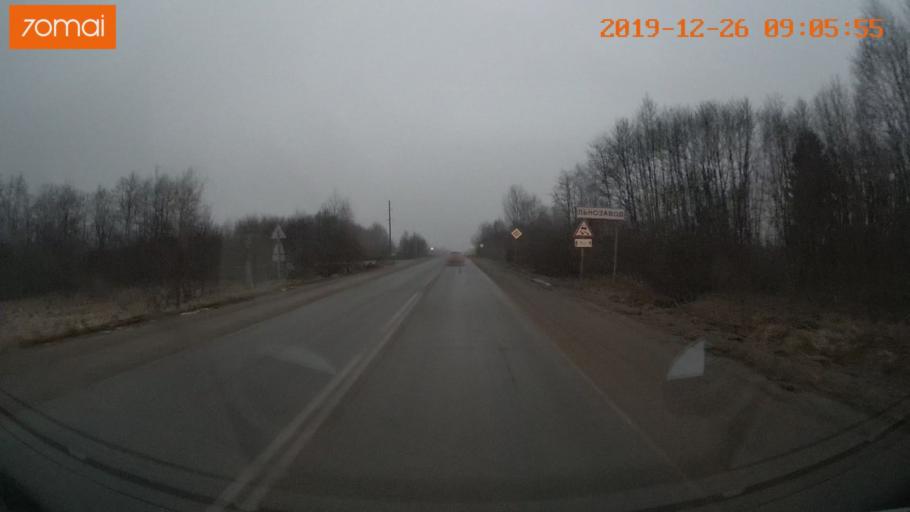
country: RU
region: Vologda
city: Gryazovets
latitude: 58.8308
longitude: 40.2559
